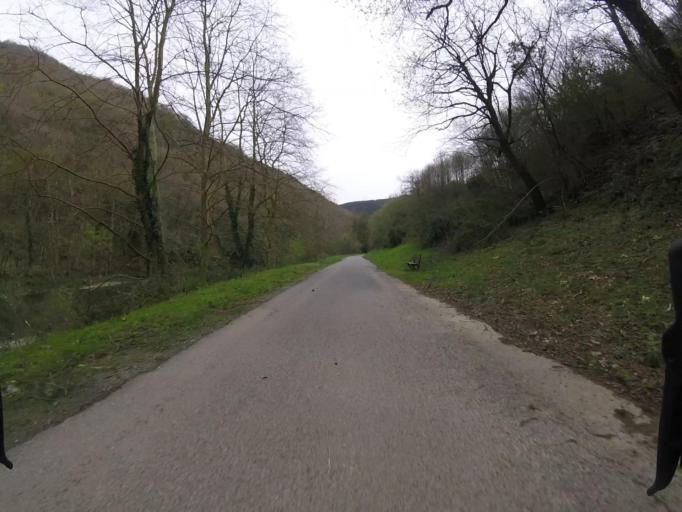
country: ES
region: Navarre
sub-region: Provincia de Navarra
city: Bera
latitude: 43.2998
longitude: -1.7324
